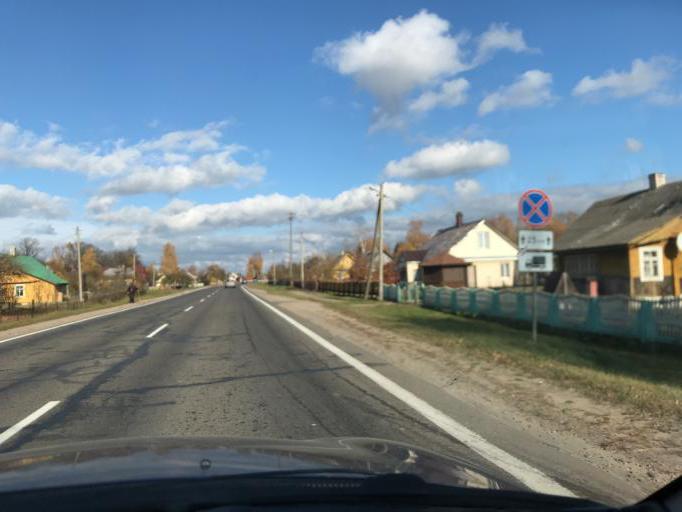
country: LT
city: Salcininkai
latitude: 54.2387
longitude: 25.3551
